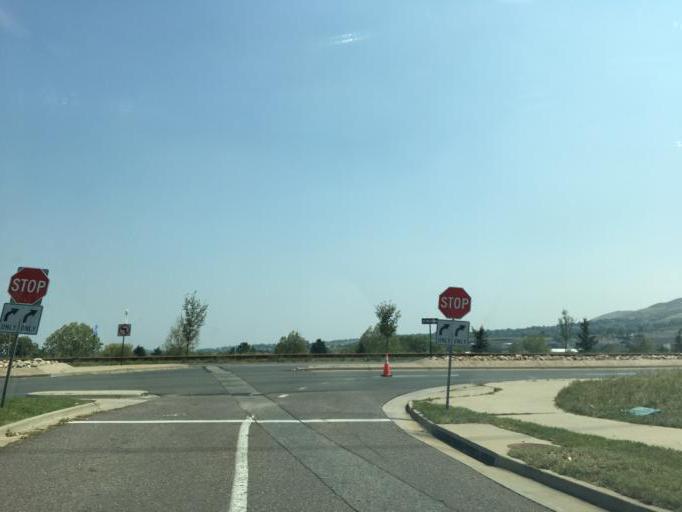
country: US
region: Colorado
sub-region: Jefferson County
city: West Pleasant View
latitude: 39.7269
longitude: -105.1990
